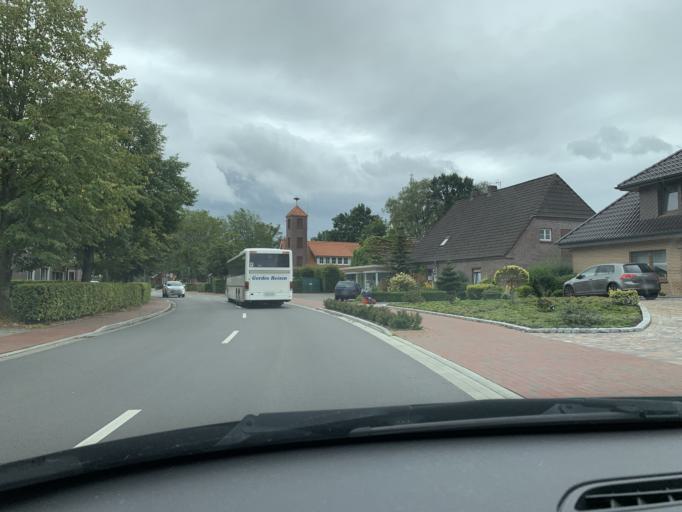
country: DE
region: Lower Saxony
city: Westerstede
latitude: 53.3152
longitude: 7.9197
